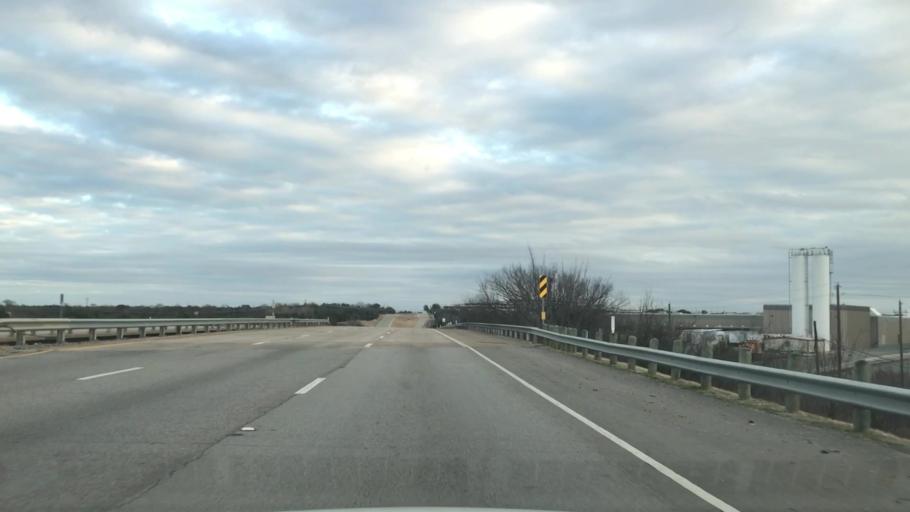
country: US
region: Texas
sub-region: Dallas County
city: Cockrell Hill
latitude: 32.7053
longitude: -96.9035
